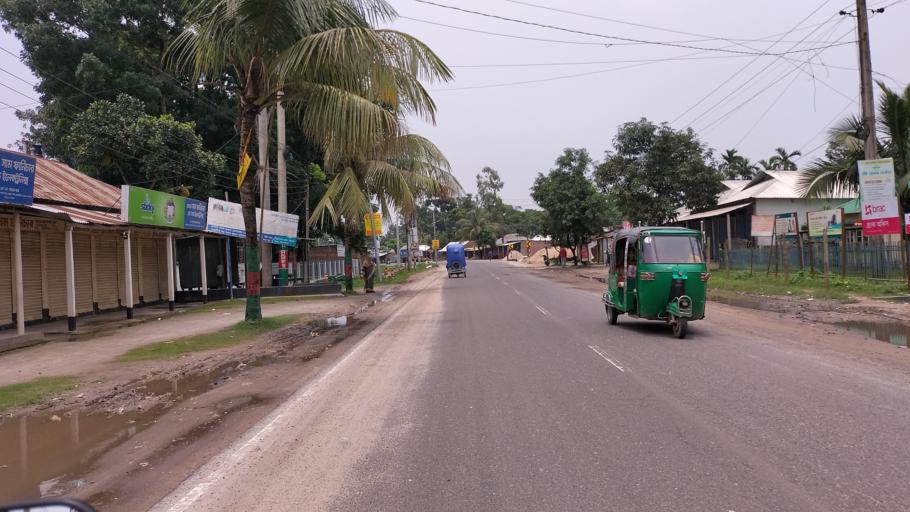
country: BD
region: Dhaka
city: Mymensingh
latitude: 24.7669
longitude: 90.4541
